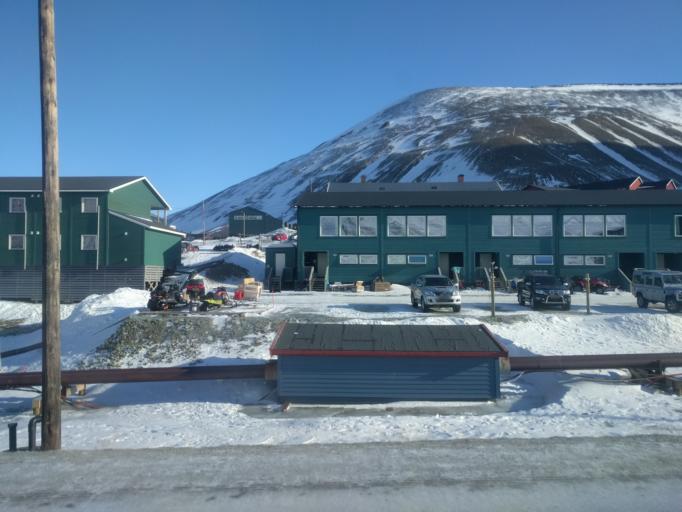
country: SJ
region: Svalbard
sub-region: Spitsbergen
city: Longyearbyen
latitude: 78.2118
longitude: 15.6162
